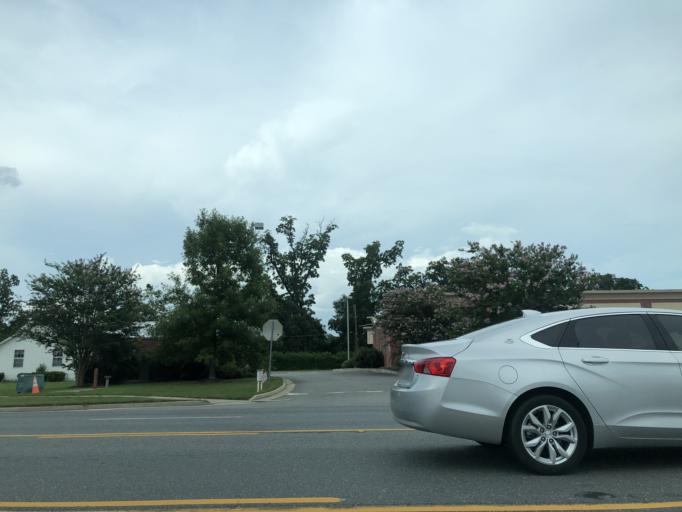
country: US
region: Georgia
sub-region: Wayne County
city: Jesup
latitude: 31.6098
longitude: -81.8838
